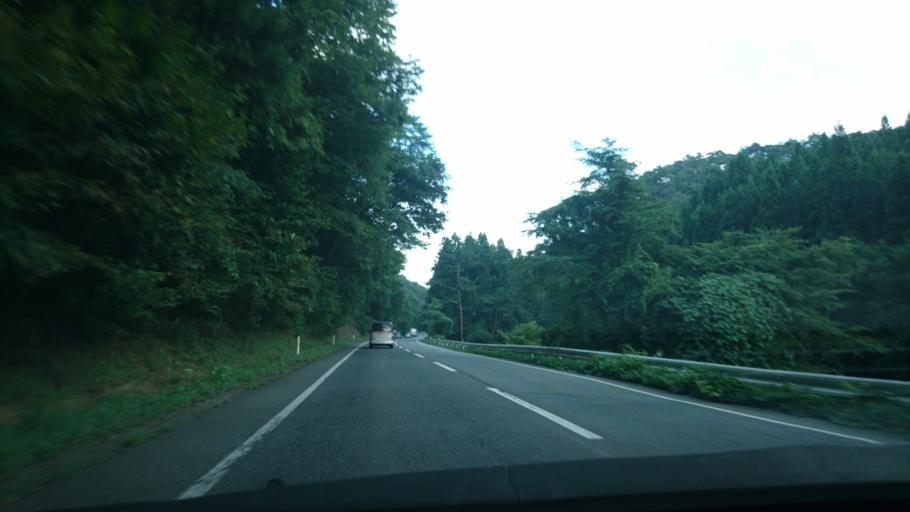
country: JP
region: Iwate
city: Mizusawa
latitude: 39.0501
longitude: 141.2301
